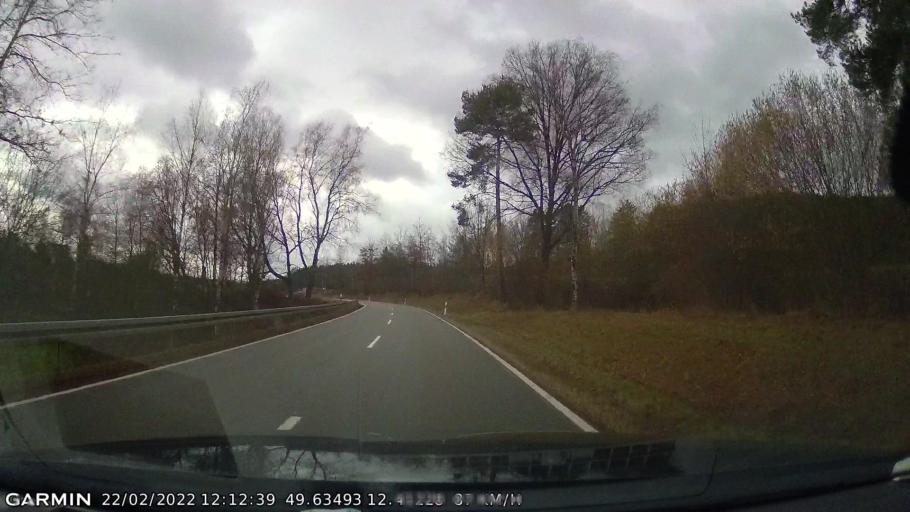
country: DE
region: Bavaria
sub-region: Upper Palatinate
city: Pleystein
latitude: 49.6346
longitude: 12.4121
